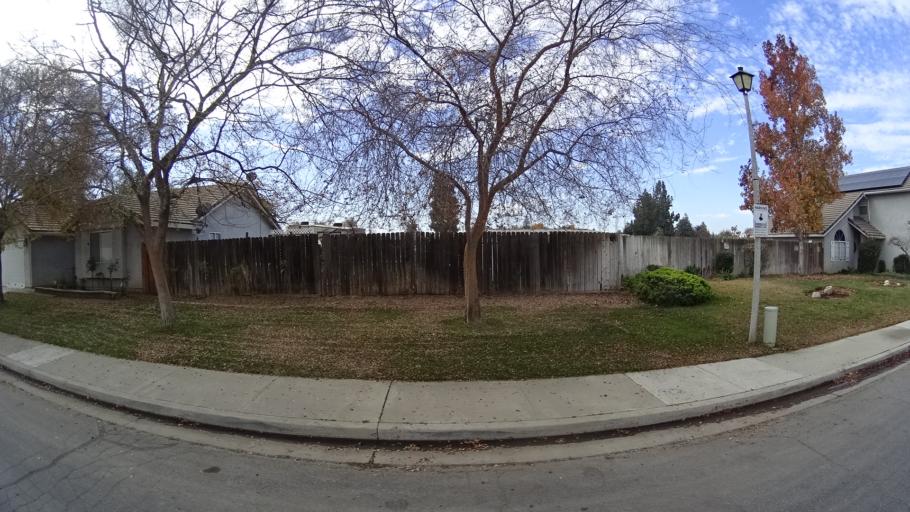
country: US
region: California
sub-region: Kern County
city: Rosedale
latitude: 35.3886
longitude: -119.1324
